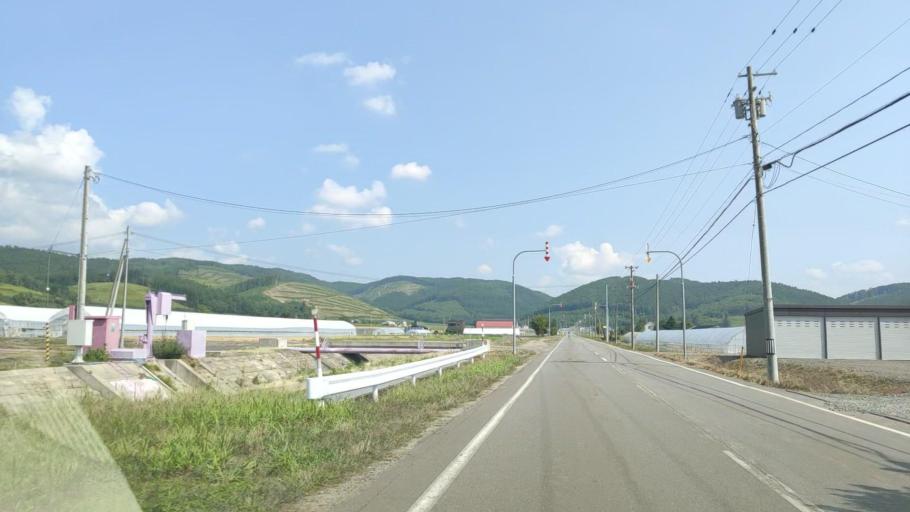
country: JP
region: Hokkaido
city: Shimo-furano
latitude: 43.4092
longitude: 142.3971
